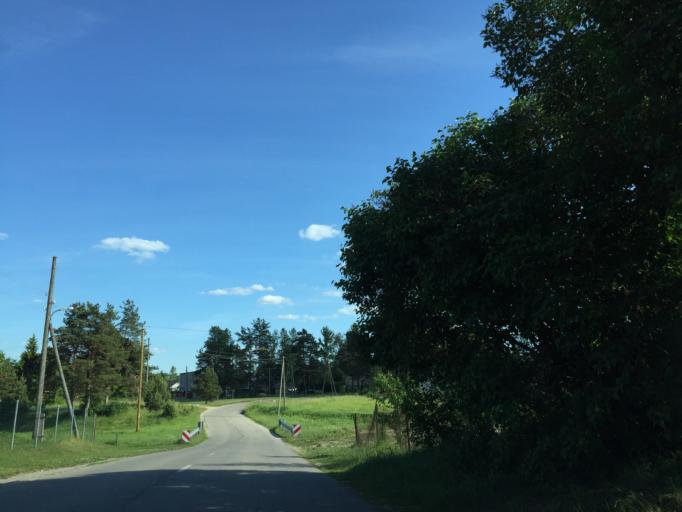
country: LV
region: Rezekne
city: Rezekne
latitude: 56.3460
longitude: 27.1665
